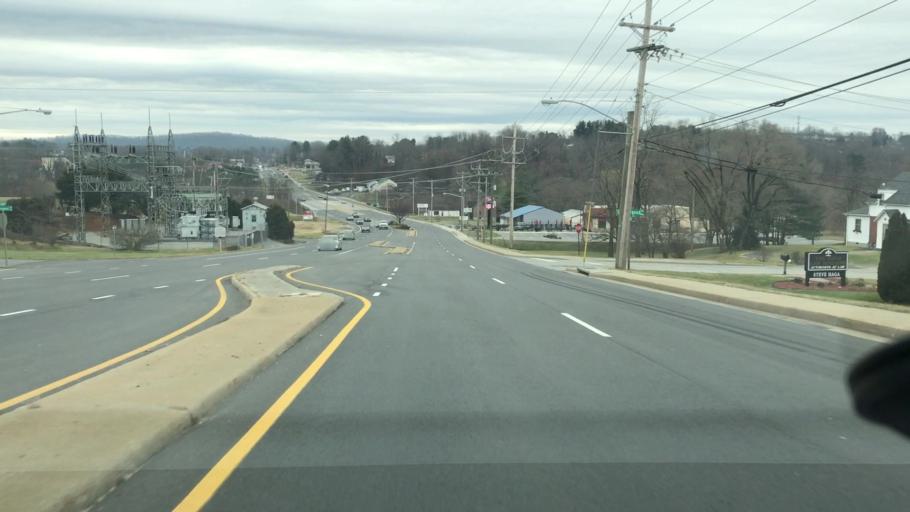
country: US
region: Virginia
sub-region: Montgomery County
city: Christiansburg
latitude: 37.1434
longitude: -80.4151
